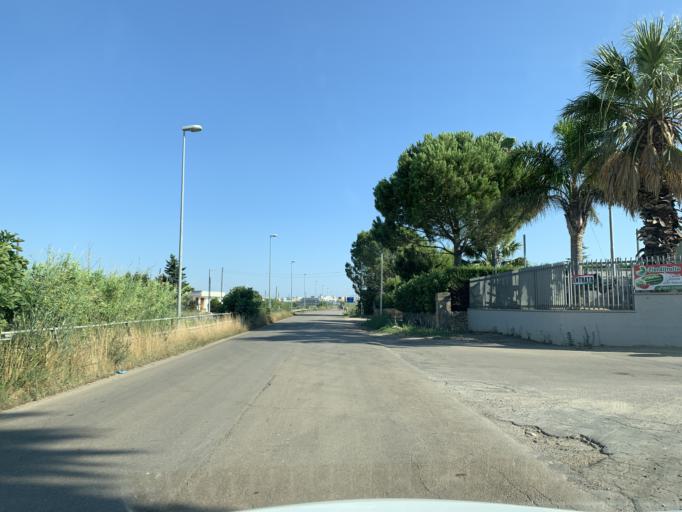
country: IT
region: Apulia
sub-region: Provincia di Lecce
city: Nardo
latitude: 40.1915
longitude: 18.0258
